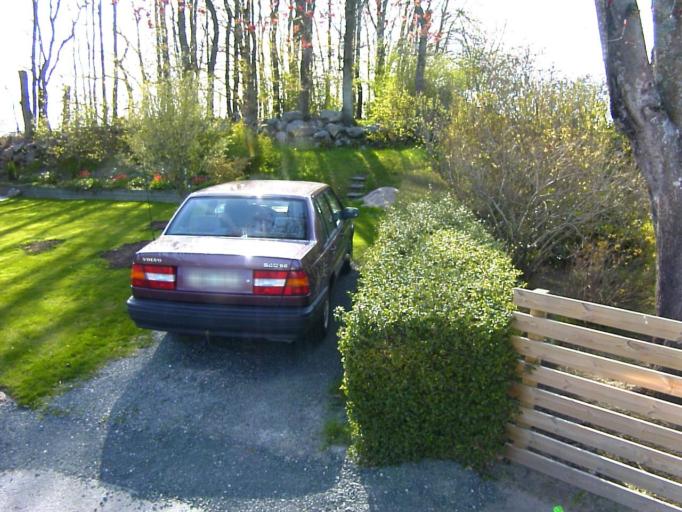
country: SE
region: Skane
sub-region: Kristianstads Kommun
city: Onnestad
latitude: 55.9948
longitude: 14.0313
